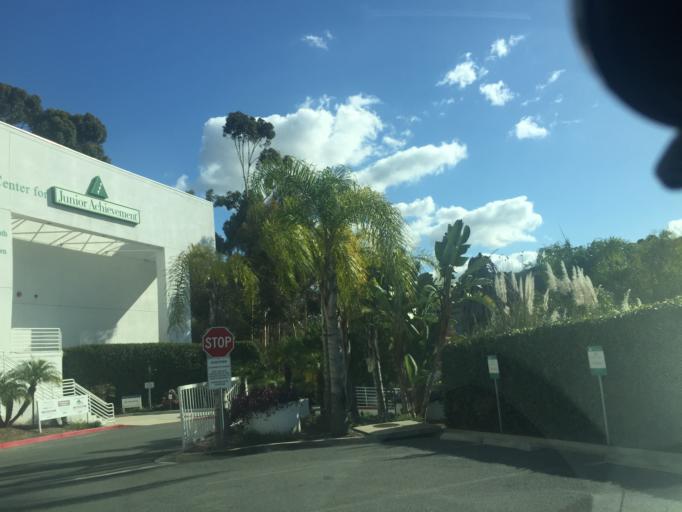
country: US
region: California
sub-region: San Diego County
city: La Mesa
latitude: 32.7827
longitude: -117.0904
